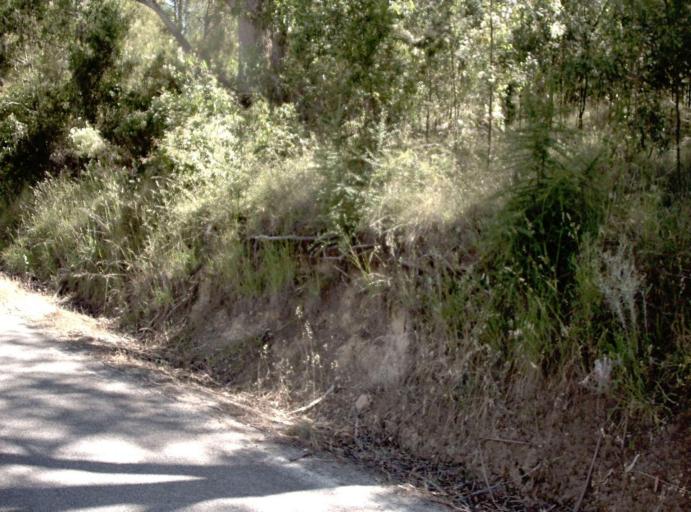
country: AU
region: Victoria
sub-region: East Gippsland
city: Lakes Entrance
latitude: -37.4557
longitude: 148.1940
